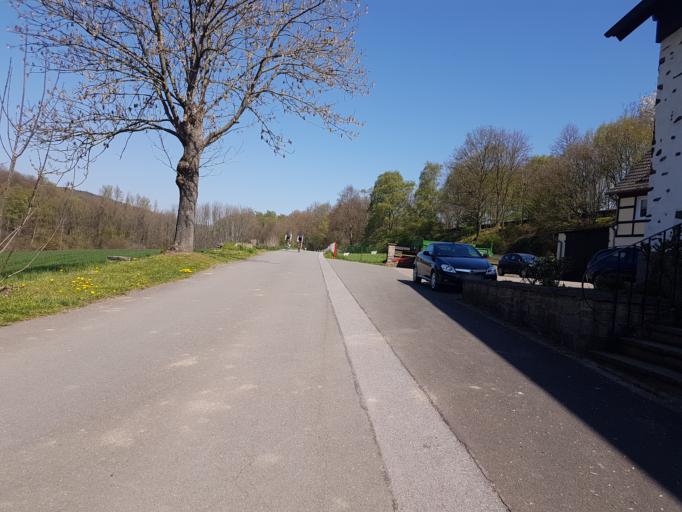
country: DE
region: North Rhine-Westphalia
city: Gevelsberg
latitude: 51.3814
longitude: 7.3104
